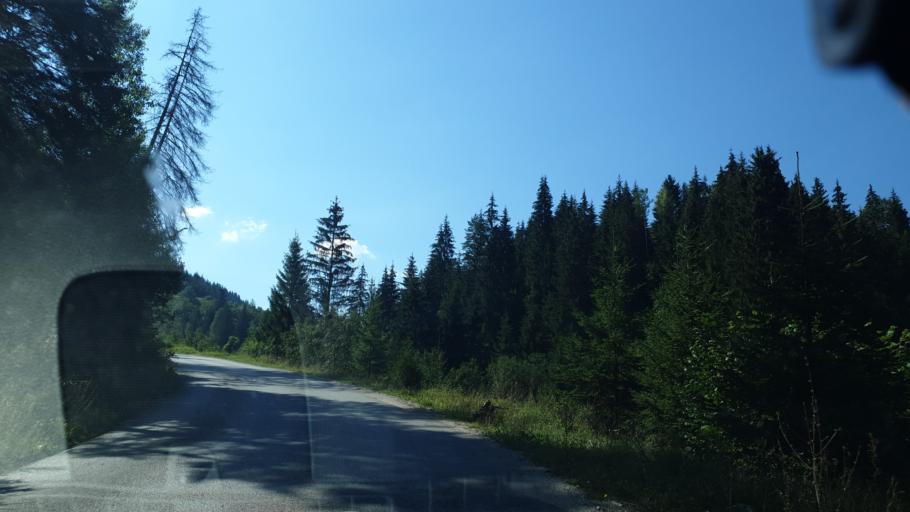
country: RS
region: Central Serbia
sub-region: Zlatiborski Okrug
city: Nova Varos
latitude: 43.4412
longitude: 19.8528
